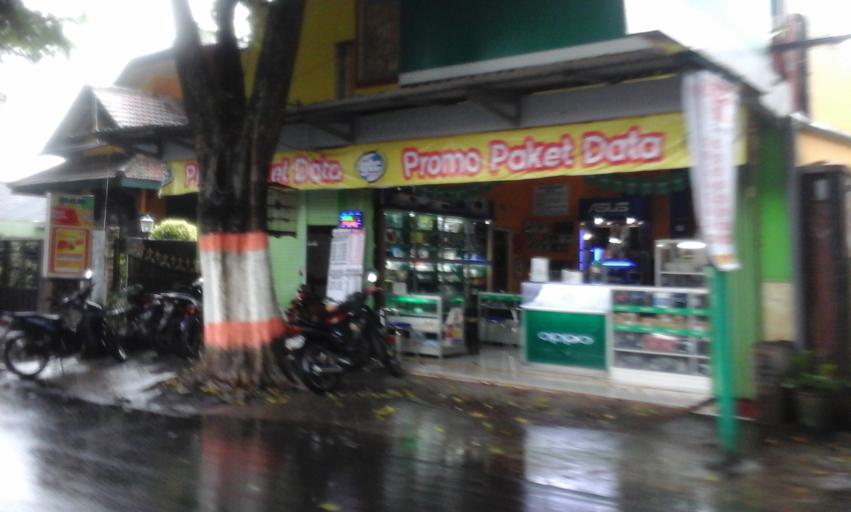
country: ID
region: East Java
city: Lumajang
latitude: -8.1358
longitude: 113.2291
